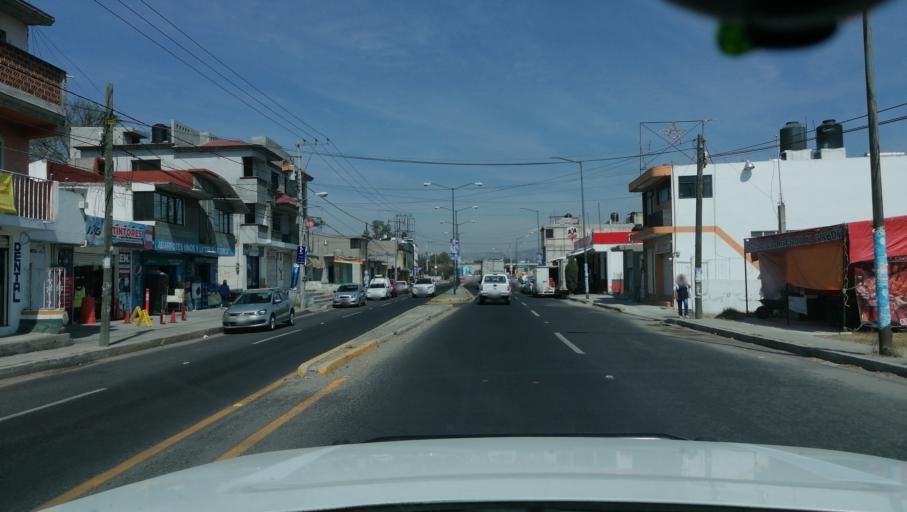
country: MX
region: Tlaxcala
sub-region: Tepeyanco
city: Santiago Tlacochcalco
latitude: 19.2811
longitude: -98.2376
